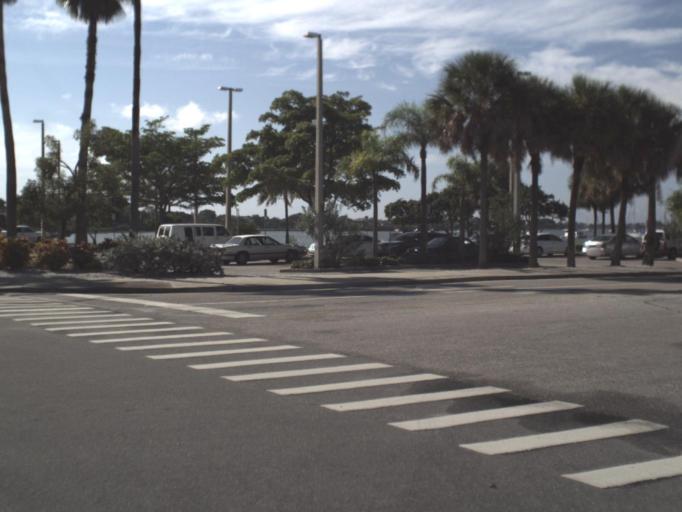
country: US
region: Florida
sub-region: Sarasota County
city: Sarasota
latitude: 27.3329
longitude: -82.5430
